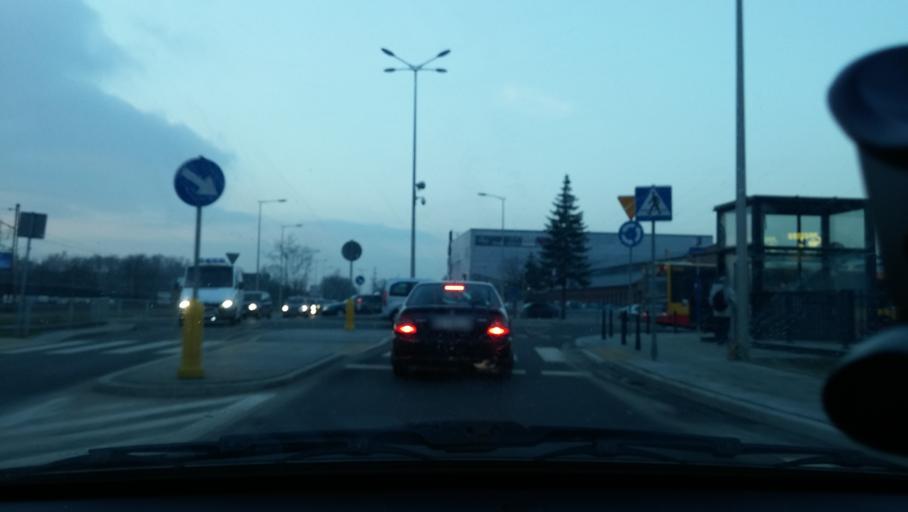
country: PL
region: Masovian Voivodeship
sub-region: Warszawa
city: Wawer
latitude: 52.2047
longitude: 21.1687
